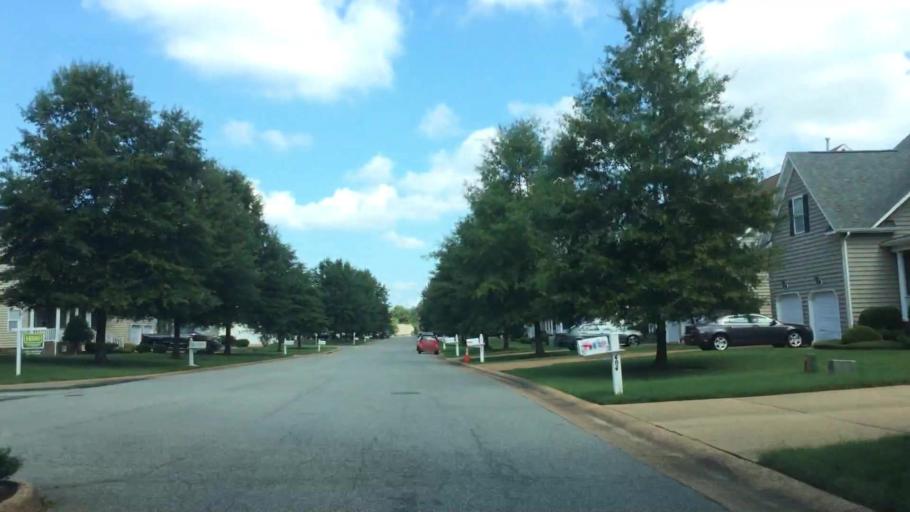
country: US
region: Virginia
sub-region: City of Williamsburg
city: Williamsburg
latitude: 37.2871
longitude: -76.6741
